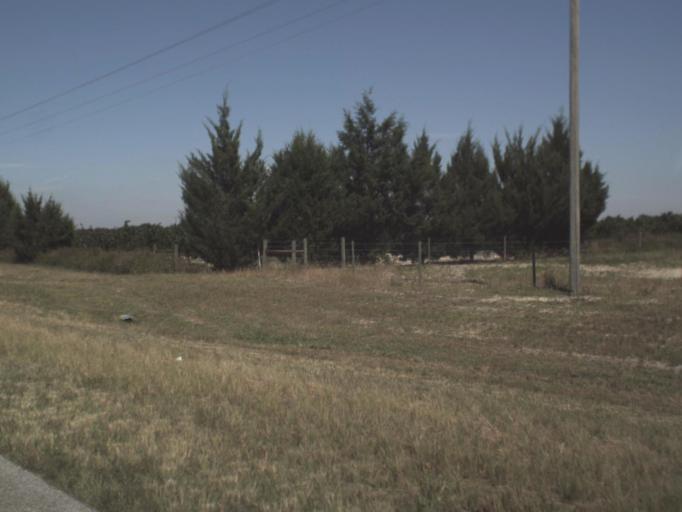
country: US
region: Florida
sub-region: Highlands County
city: Placid Lakes
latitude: 27.1677
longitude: -81.3286
